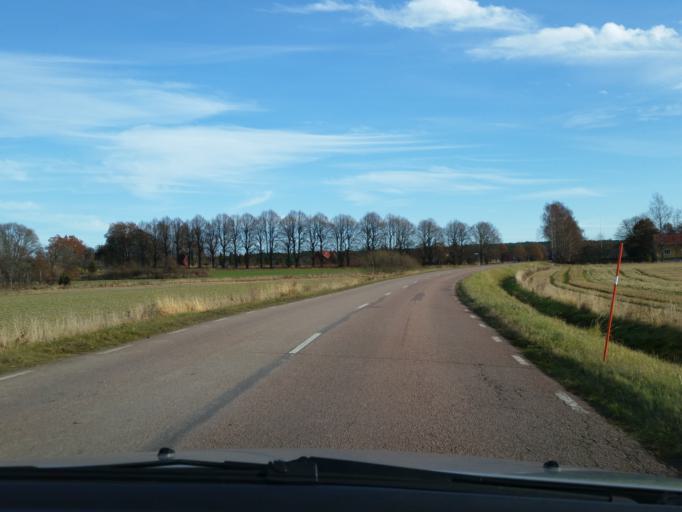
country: AX
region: Alands landsbygd
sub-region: Saltvik
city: Saltvik
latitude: 60.3215
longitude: 20.0138
